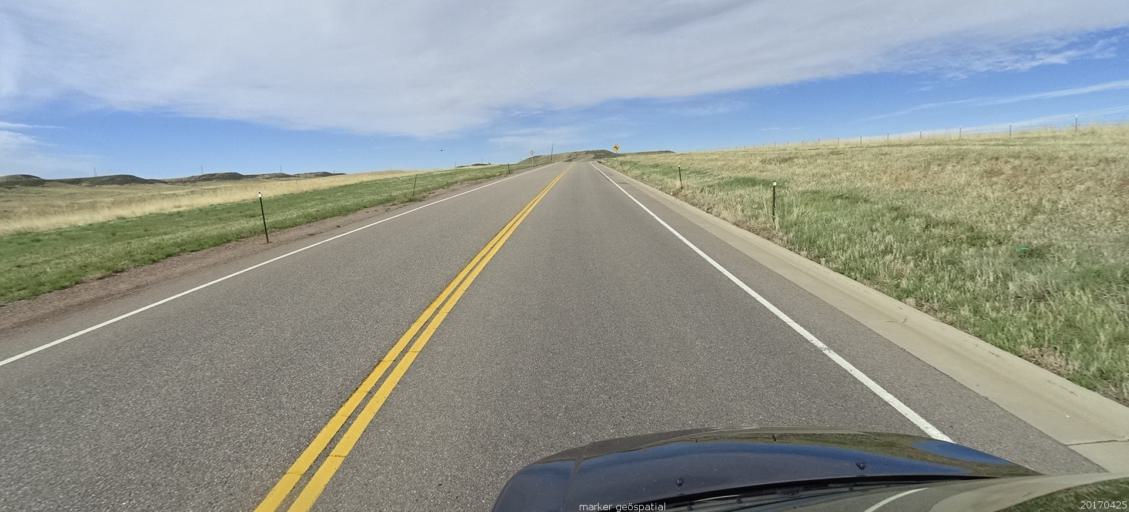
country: US
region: Colorado
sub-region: Douglas County
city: Meridian
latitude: 39.5277
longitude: -104.8530
